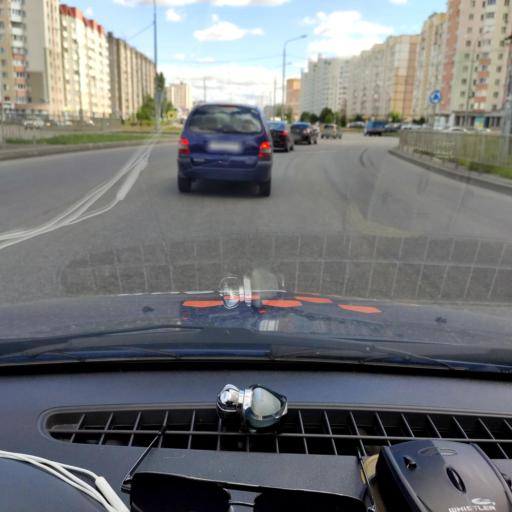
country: RU
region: Lipetsk
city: Syrskoye
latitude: 52.5811
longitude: 39.5134
